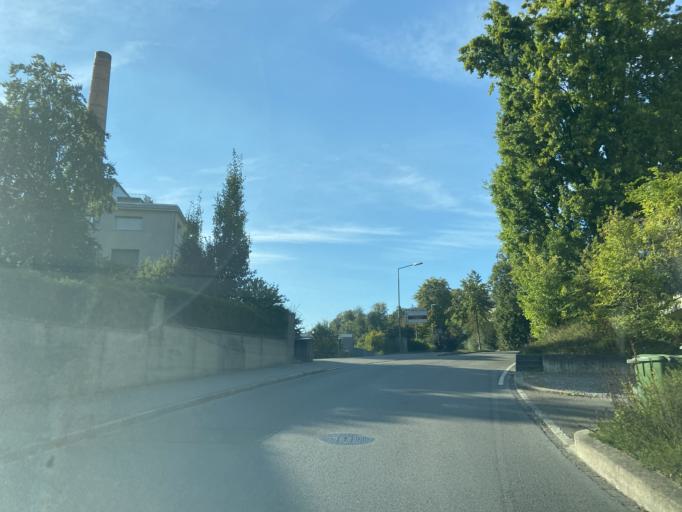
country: CH
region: Zurich
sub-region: Bezirk Winterthur
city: Stadt Winterthur (Kreis 1) / Lind
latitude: 47.5087
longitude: 8.7316
